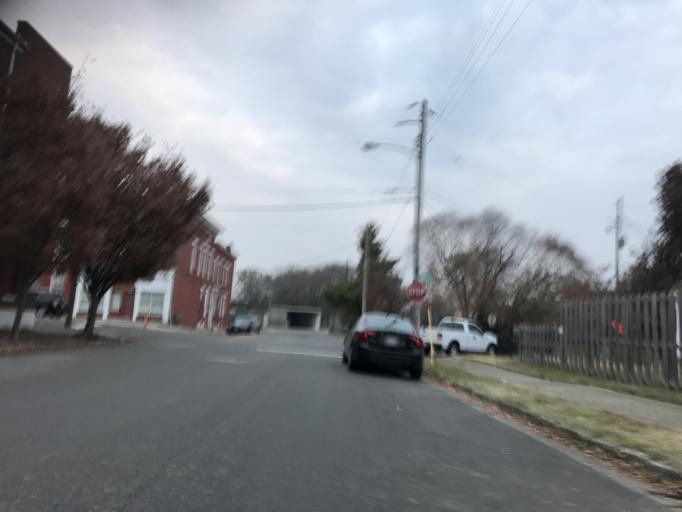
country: US
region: Indiana
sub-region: Clark County
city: Jeffersonville
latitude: 38.2556
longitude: -85.7335
